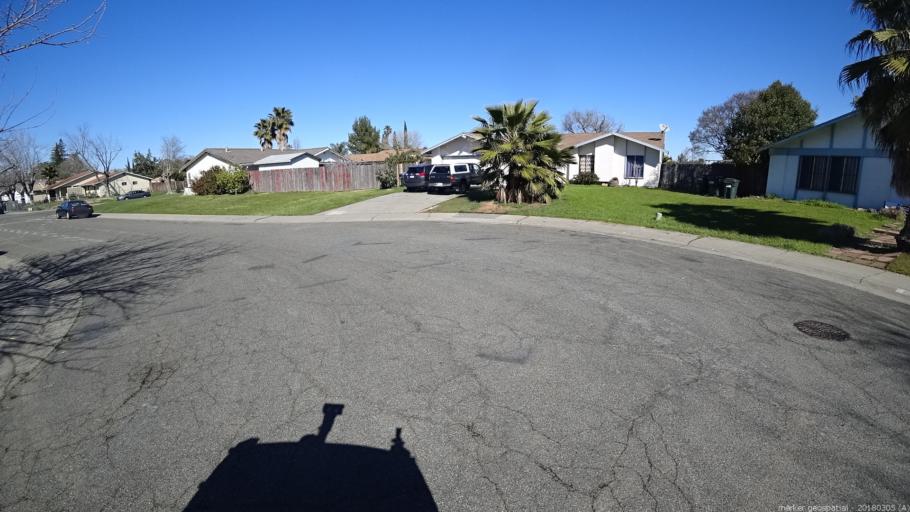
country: US
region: California
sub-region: Sacramento County
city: Florin
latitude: 38.4892
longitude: -121.4192
